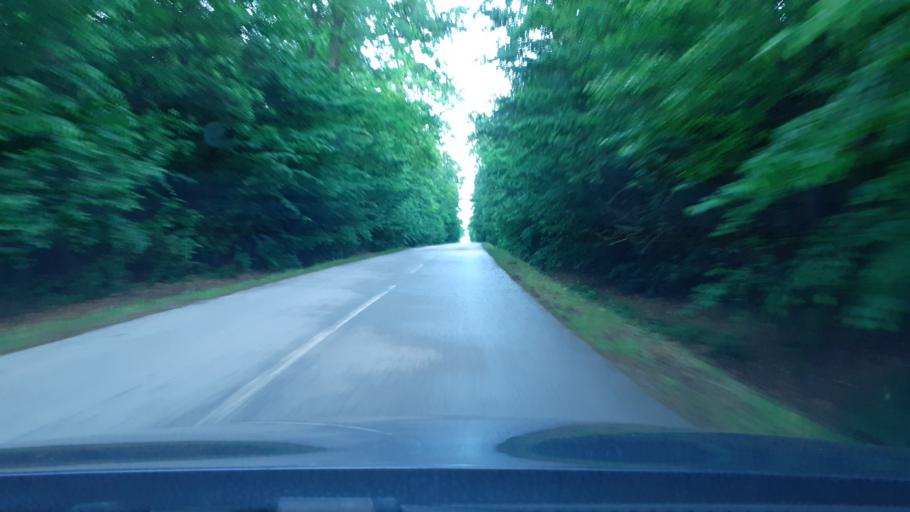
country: HR
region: Pozesko-Slavonska
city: Jaksic
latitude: 45.3479
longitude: 17.7871
